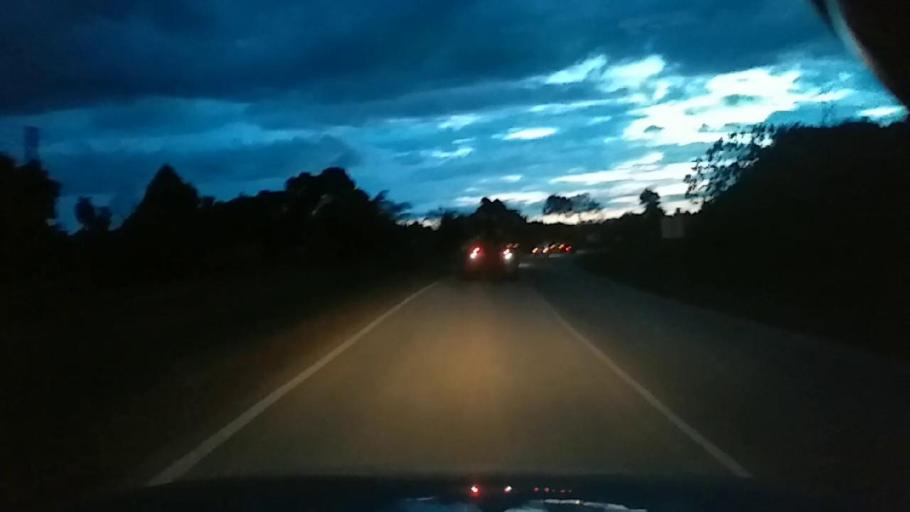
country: MY
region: Sarawak
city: Sibu
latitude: 2.4134
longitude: 112.1637
